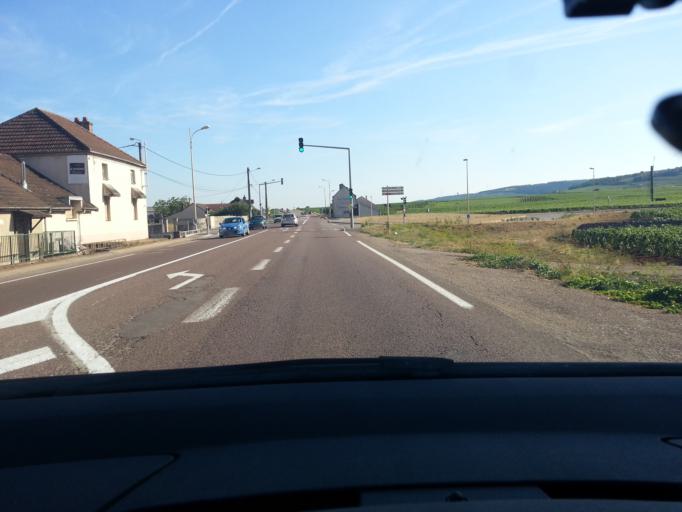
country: FR
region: Bourgogne
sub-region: Departement de la Cote-d'Or
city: Gevrey-Chambertin
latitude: 47.1946
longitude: 4.9690
